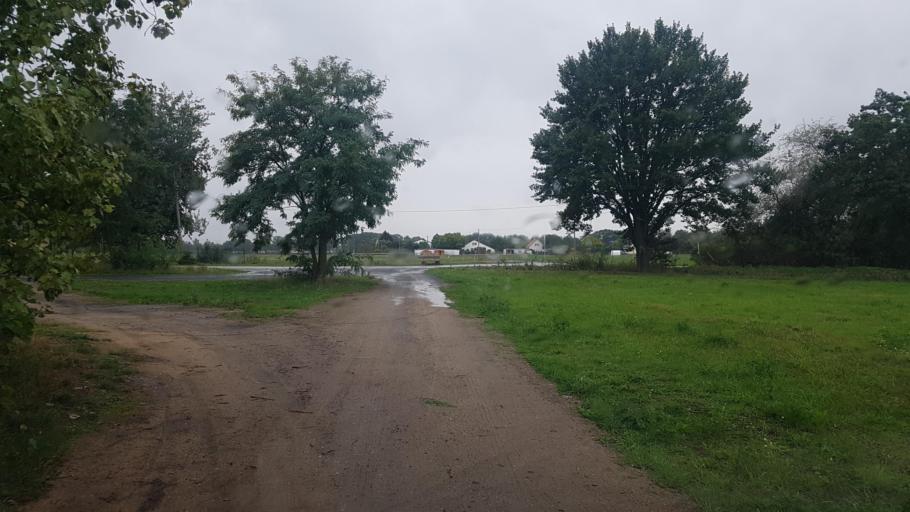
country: DE
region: Brandenburg
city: Elsterwerda
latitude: 51.4607
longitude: 13.5007
